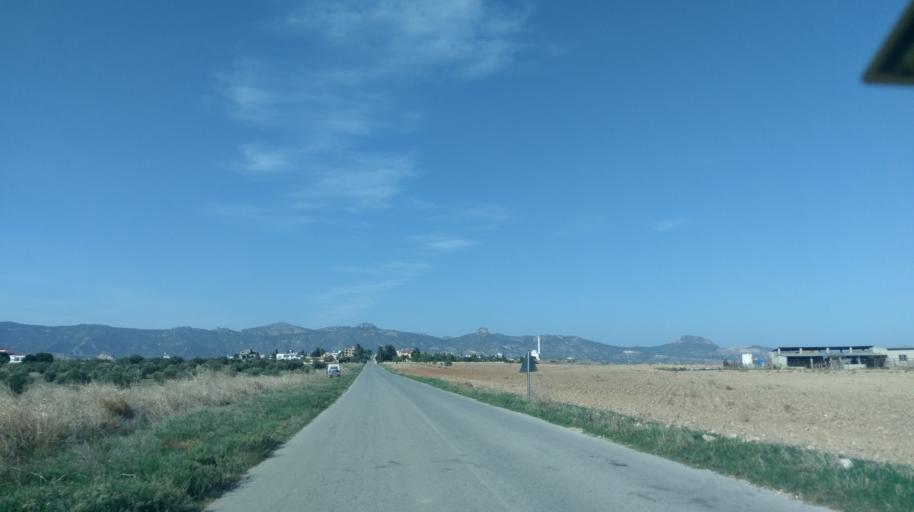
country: CY
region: Ammochostos
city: Trikomo
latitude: 35.3481
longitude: 33.9671
